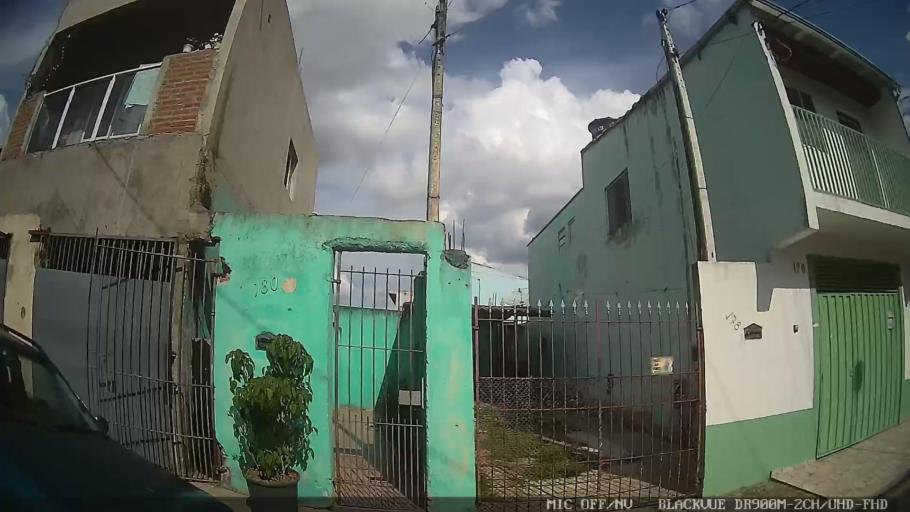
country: BR
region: Sao Paulo
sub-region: Atibaia
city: Atibaia
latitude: -23.1195
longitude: -46.5772
